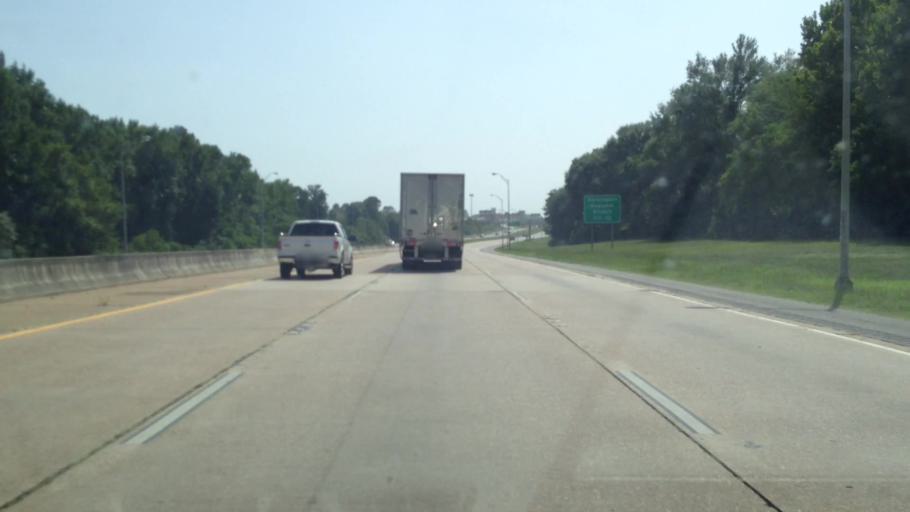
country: US
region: Louisiana
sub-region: Caddo Parish
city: Shreveport
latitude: 32.4658
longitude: -93.8163
